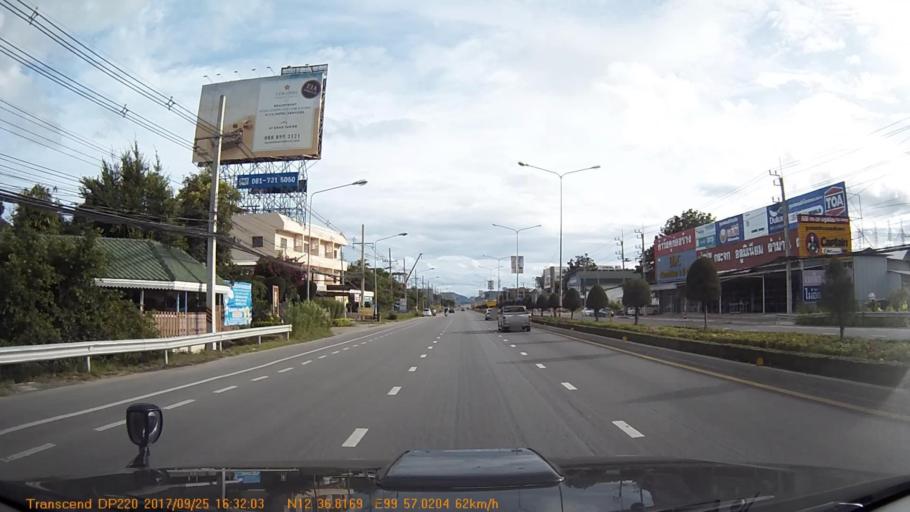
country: TH
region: Prachuap Khiri Khan
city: Hua Hin
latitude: 12.6131
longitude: 99.9503
